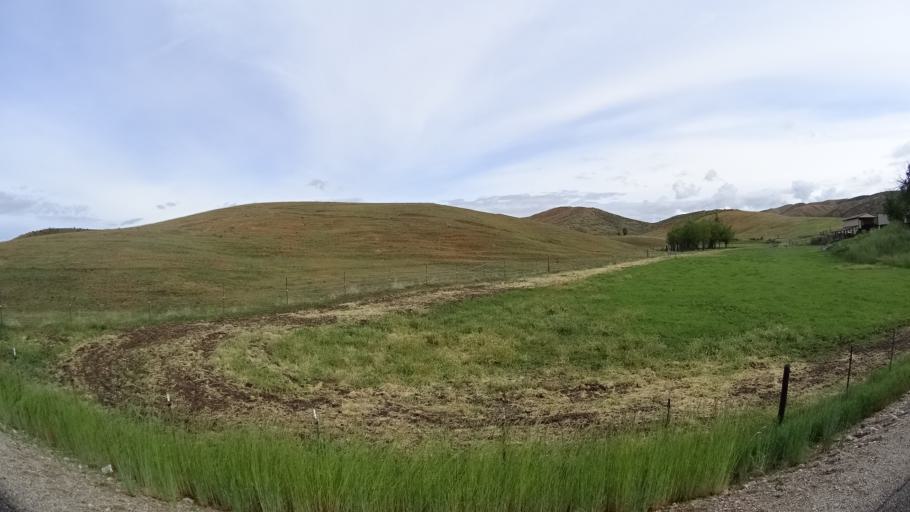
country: US
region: Idaho
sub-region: Ada County
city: Eagle
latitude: 43.7315
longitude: -116.3163
